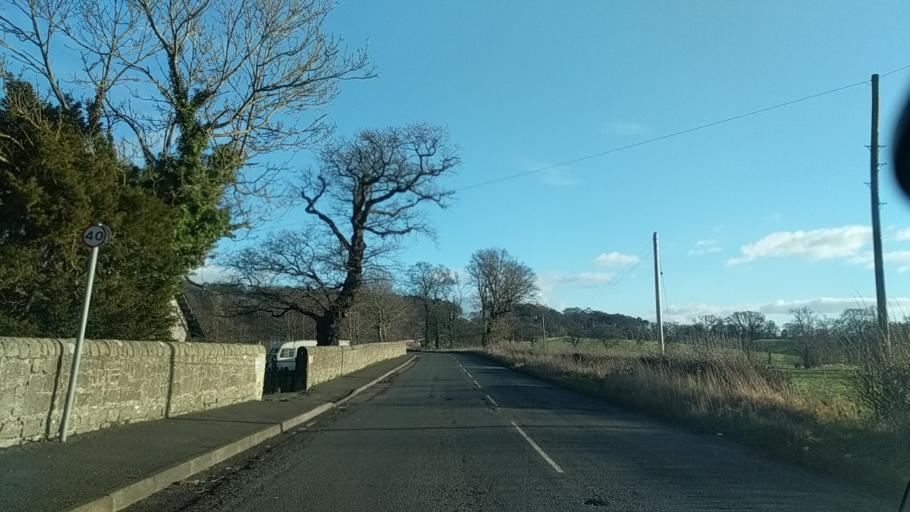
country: GB
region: Scotland
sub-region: Edinburgh
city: Queensferry
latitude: 55.9890
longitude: -3.3752
